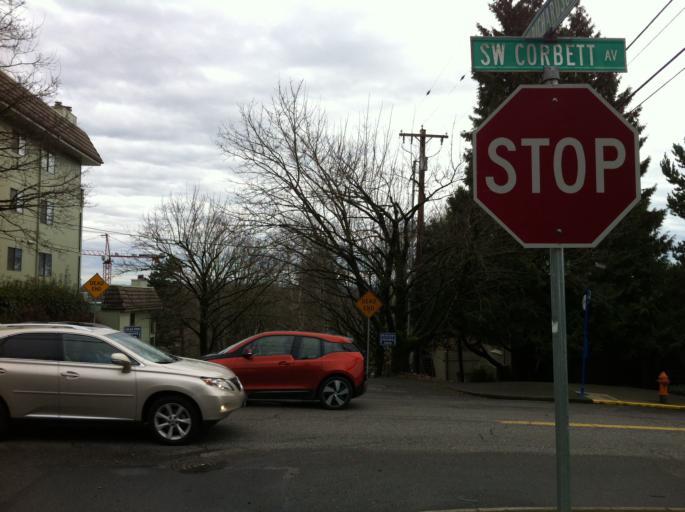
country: US
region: Oregon
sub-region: Multnomah County
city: Portland
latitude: 45.4872
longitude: -122.6769
